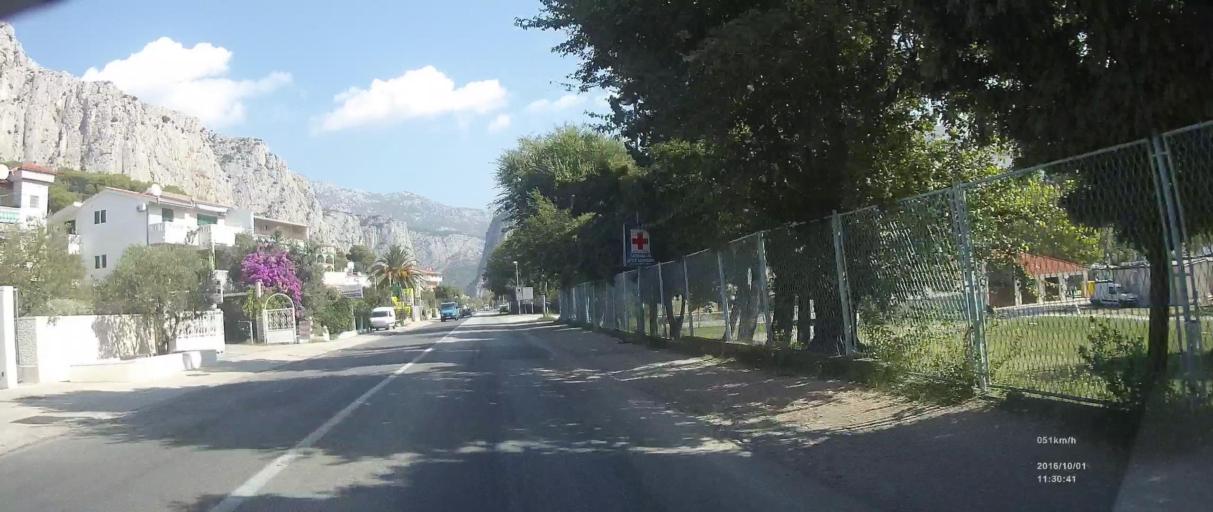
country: HR
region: Splitsko-Dalmatinska
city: Duce
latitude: 43.4405
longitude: 16.6785
